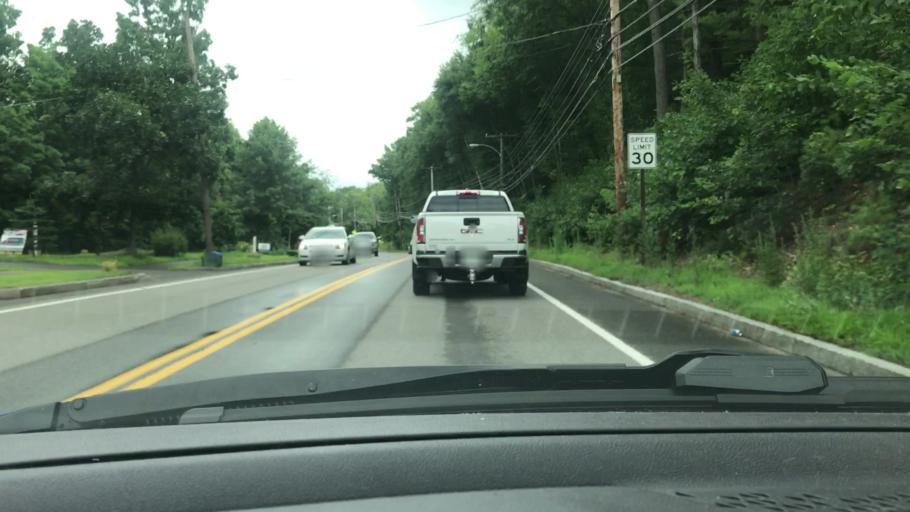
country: US
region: New Hampshire
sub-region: Merrimack County
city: East Concord
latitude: 43.2351
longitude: -71.5632
